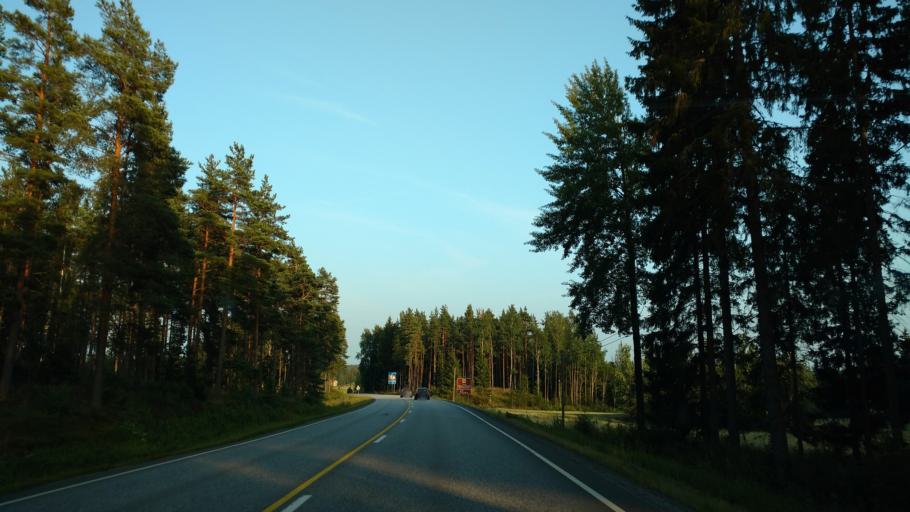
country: FI
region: Varsinais-Suomi
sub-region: Salo
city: Saerkisalo
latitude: 60.1766
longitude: 22.9527
